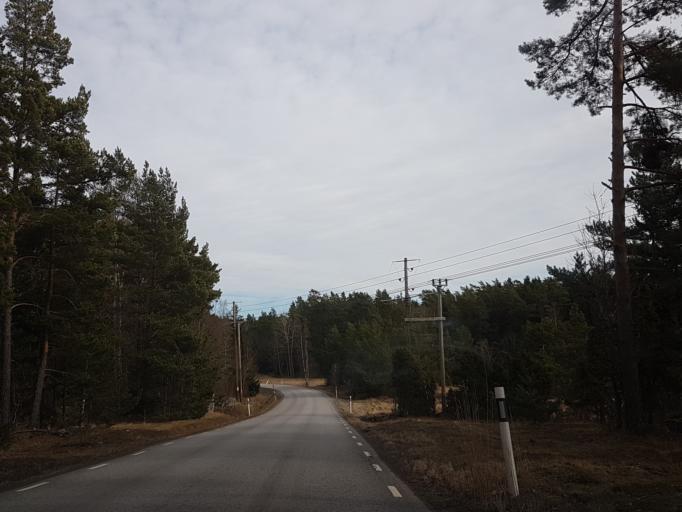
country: SE
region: Stockholm
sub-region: Norrtalje Kommun
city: Bjorko
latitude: 59.6668
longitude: 18.8549
